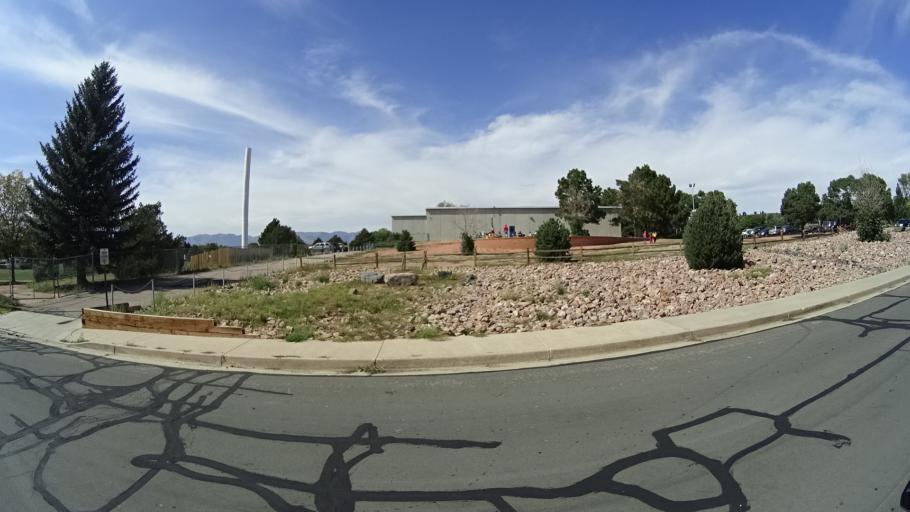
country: US
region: Colorado
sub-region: El Paso County
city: Cimarron Hills
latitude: 38.9030
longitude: -104.7560
